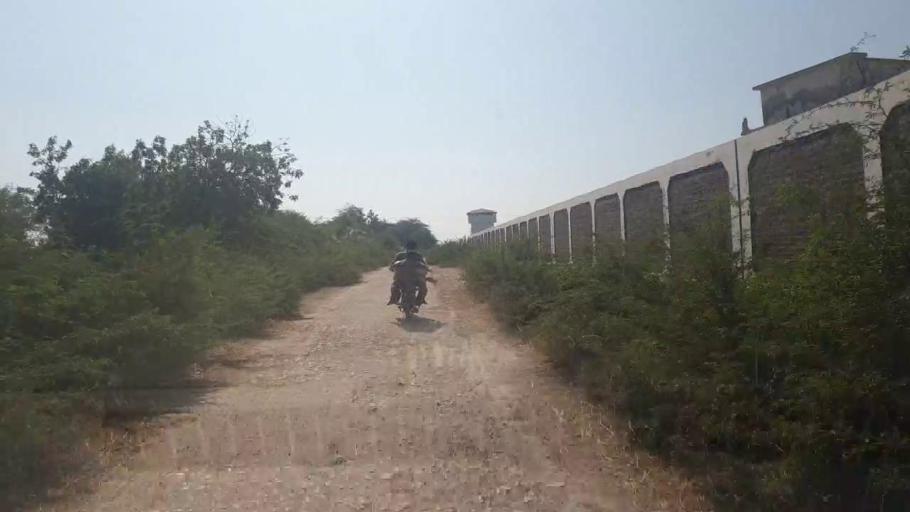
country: PK
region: Sindh
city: Badin
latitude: 24.6719
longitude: 68.8819
